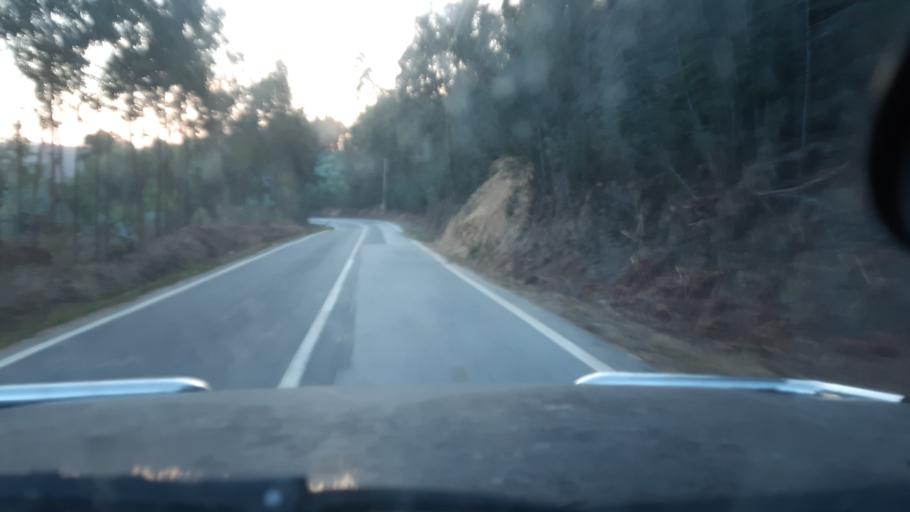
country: PT
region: Aveiro
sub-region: Agueda
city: Aguada de Cima
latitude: 40.5653
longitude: -8.3873
